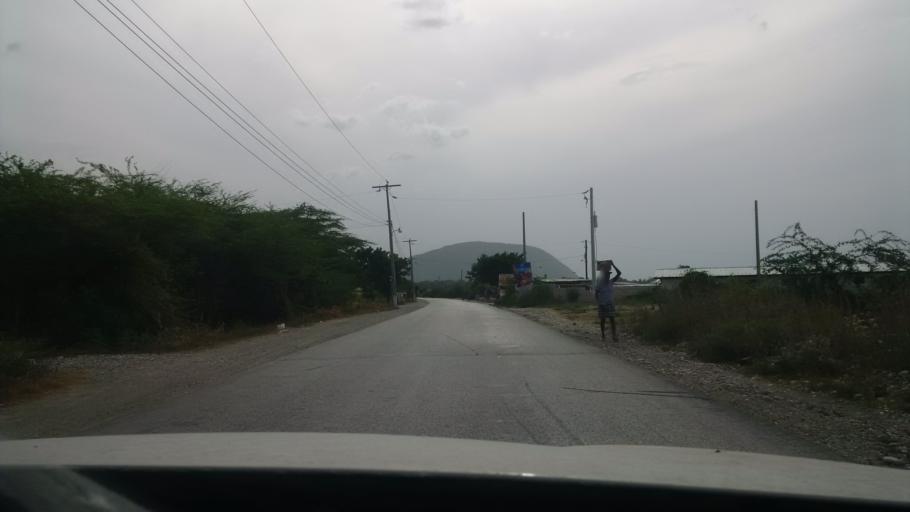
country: HT
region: Ouest
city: Grangwav
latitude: 18.4252
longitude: -72.7481
